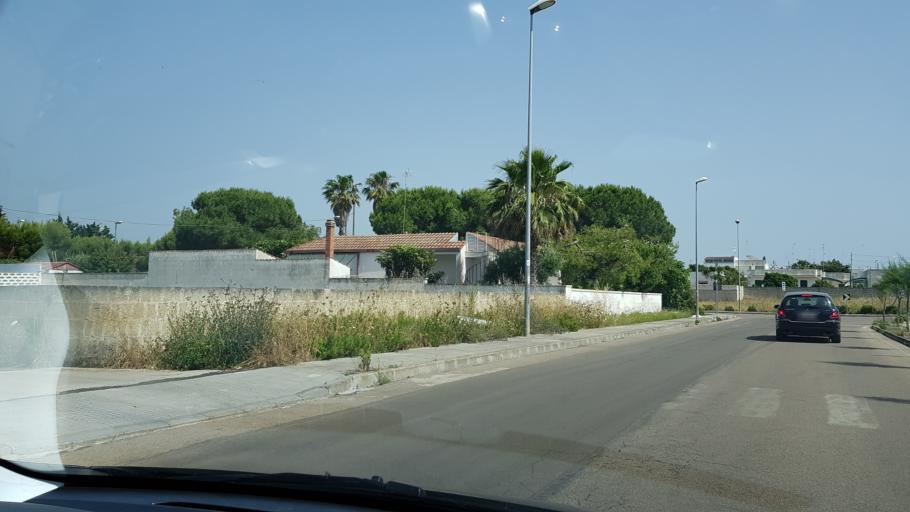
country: IT
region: Apulia
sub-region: Provincia di Lecce
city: Porto Cesareo
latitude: 40.2676
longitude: 17.8894
